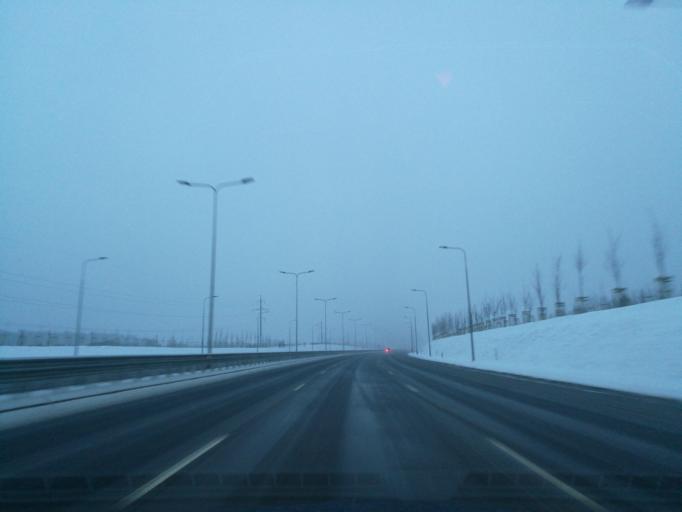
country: LT
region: Vilnius County
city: Justiniskes
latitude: 54.7120
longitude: 25.2086
